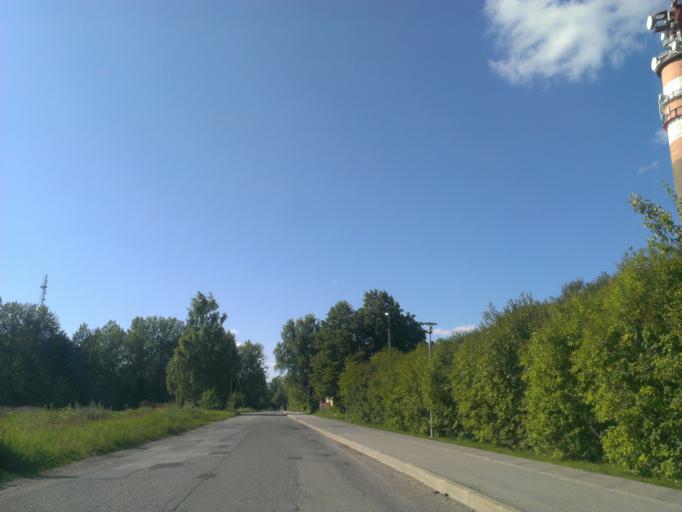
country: LV
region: Sigulda
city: Sigulda
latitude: 57.1625
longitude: 24.8814
